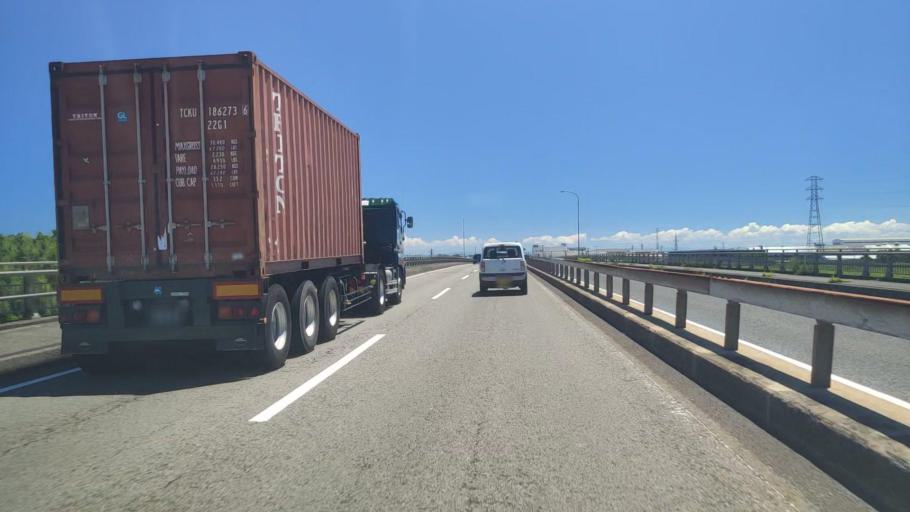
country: JP
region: Mie
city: Suzuka
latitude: 34.9081
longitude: 136.6053
